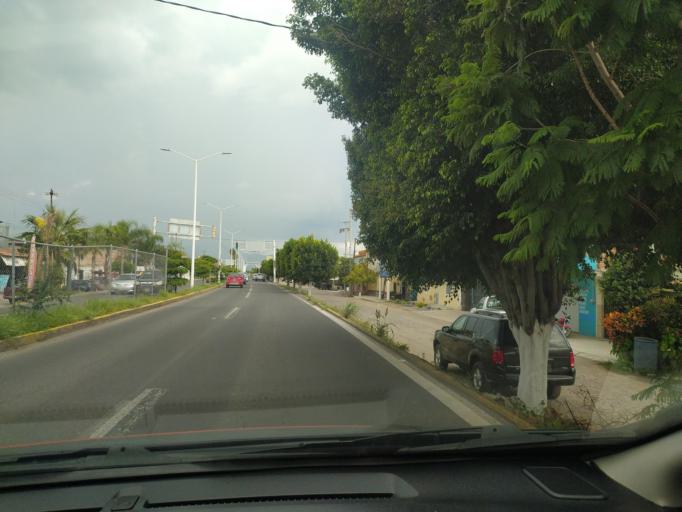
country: MX
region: Jalisco
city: Villa Corona
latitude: 20.4139
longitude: -103.6659
